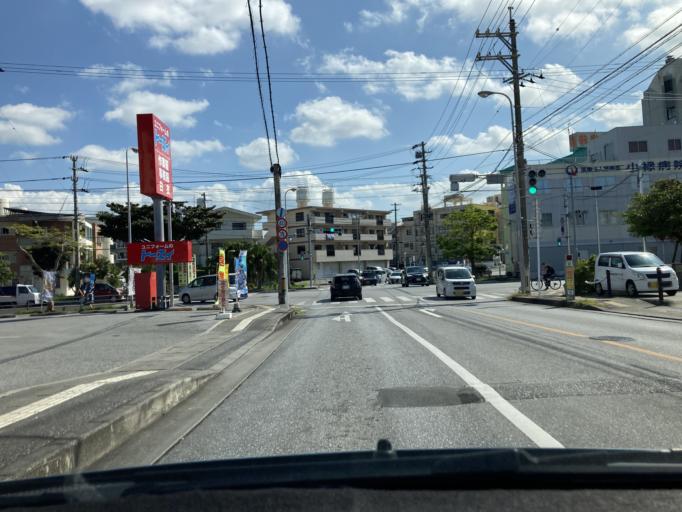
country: JP
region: Okinawa
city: Tomigusuku
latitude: 26.1940
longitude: 127.6757
